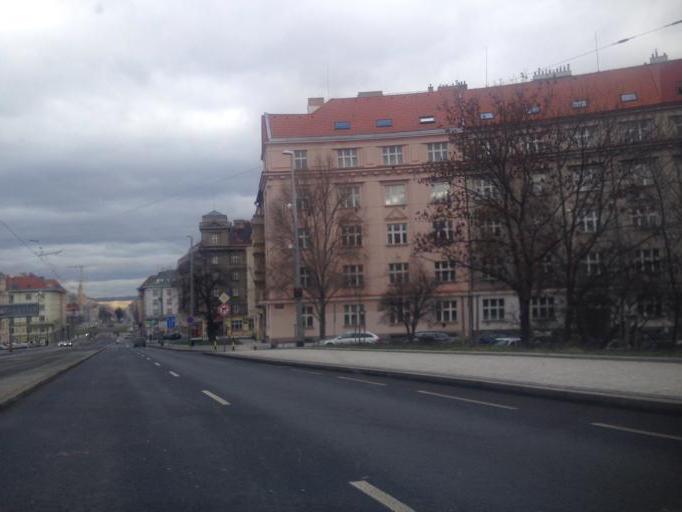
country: CZ
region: Praha
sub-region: Praha 1
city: Mala Strana
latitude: 50.0969
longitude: 14.3960
